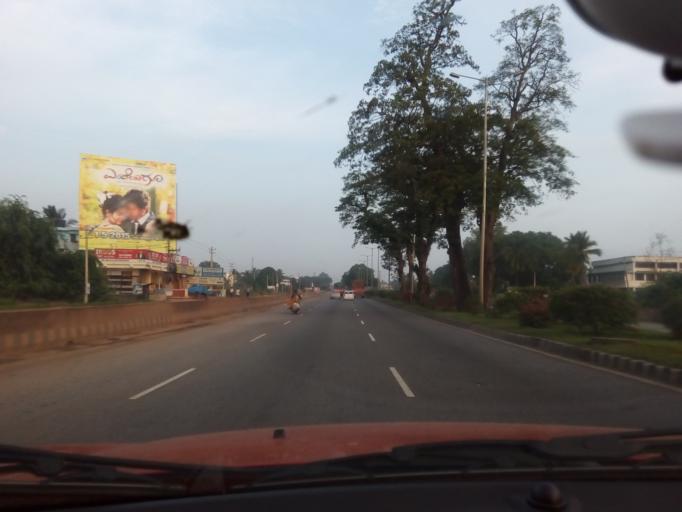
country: IN
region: Karnataka
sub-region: Bangalore Rural
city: Nelamangala
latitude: 13.0709
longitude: 77.4439
